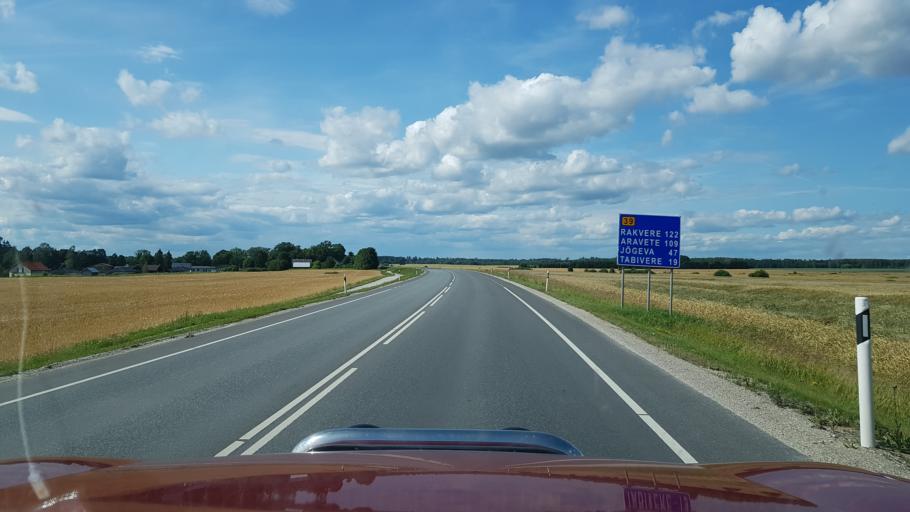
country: EE
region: Tartu
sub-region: Tartu linn
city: Tartu
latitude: 58.4118
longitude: 26.7074
